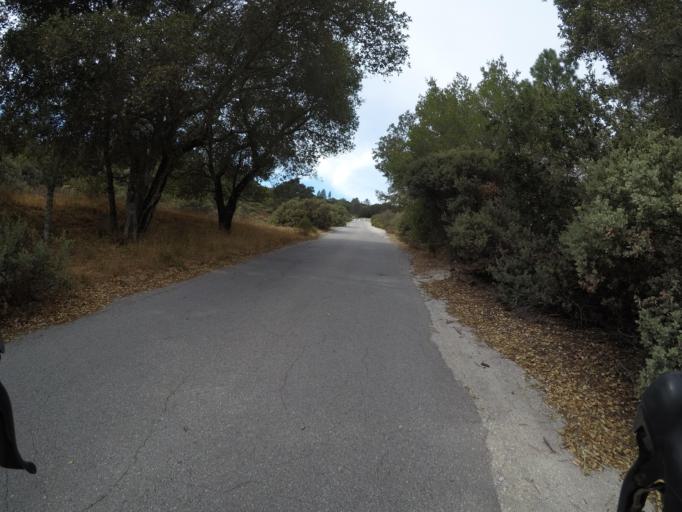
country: US
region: California
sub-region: Santa Cruz County
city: Mount Hermon
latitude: 37.0679
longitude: -122.0637
